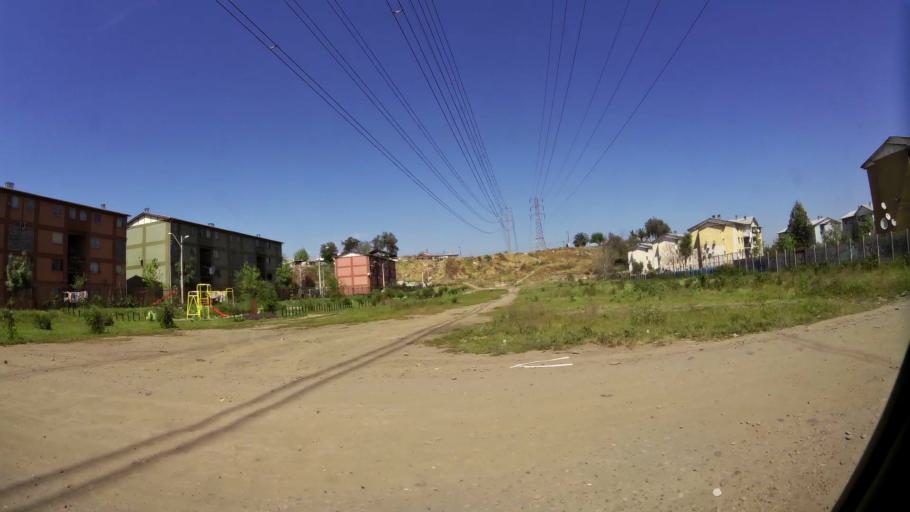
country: CL
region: Santiago Metropolitan
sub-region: Provincia de Santiago
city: Lo Prado
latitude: -33.4851
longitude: -70.7315
